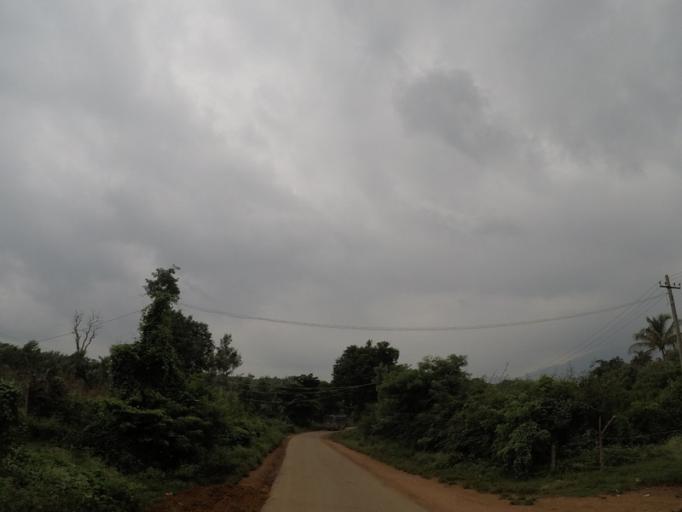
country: IN
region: Karnataka
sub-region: Chikmagalur
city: Tarikere
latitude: 13.5668
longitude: 75.7980
